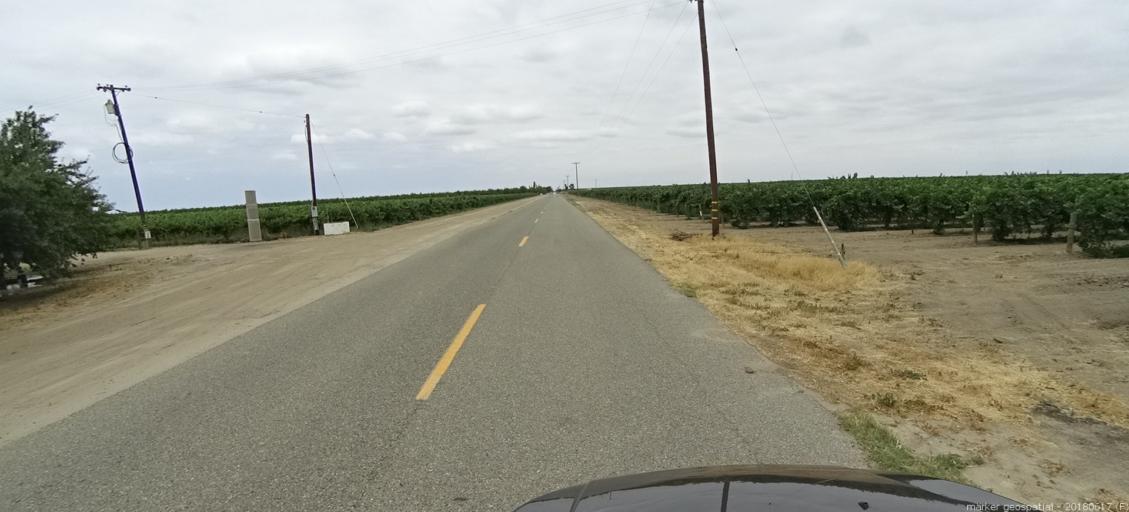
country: US
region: California
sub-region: Madera County
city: Madera
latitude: 36.9271
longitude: -120.1560
